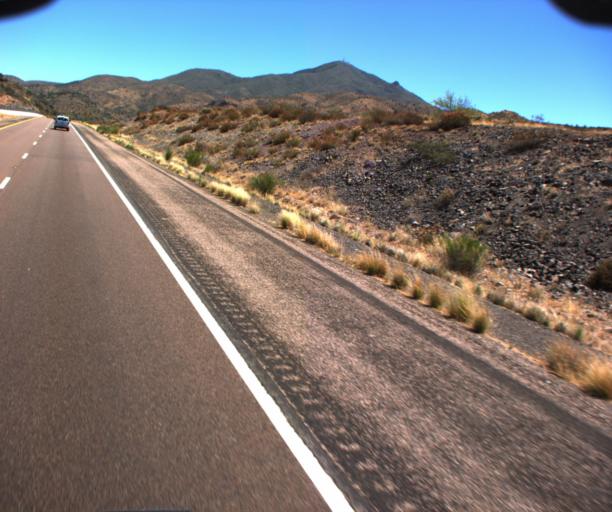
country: US
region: Arizona
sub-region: Gila County
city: Tonto Basin
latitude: 33.8732
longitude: -111.4620
